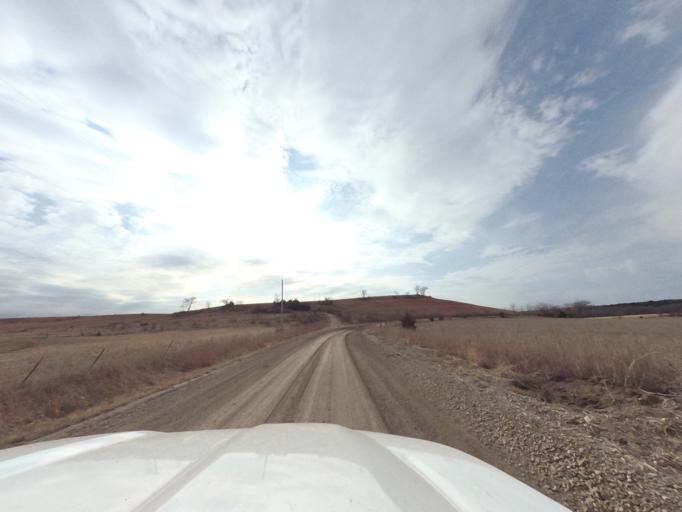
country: US
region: Kansas
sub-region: Chase County
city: Cottonwood Falls
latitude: 38.2859
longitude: -96.7320
